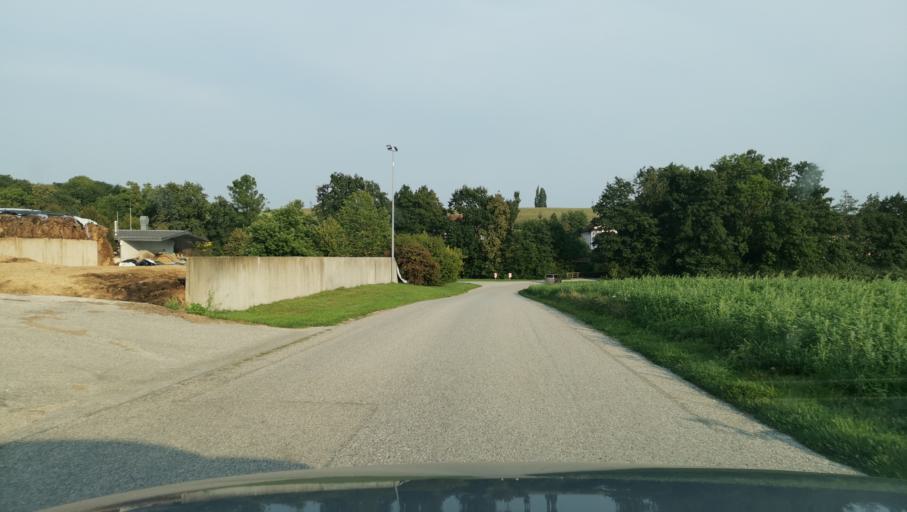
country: AT
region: Upper Austria
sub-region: Politischer Bezirk Grieskirchen
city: Grieskirchen
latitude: 48.2888
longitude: 13.8086
